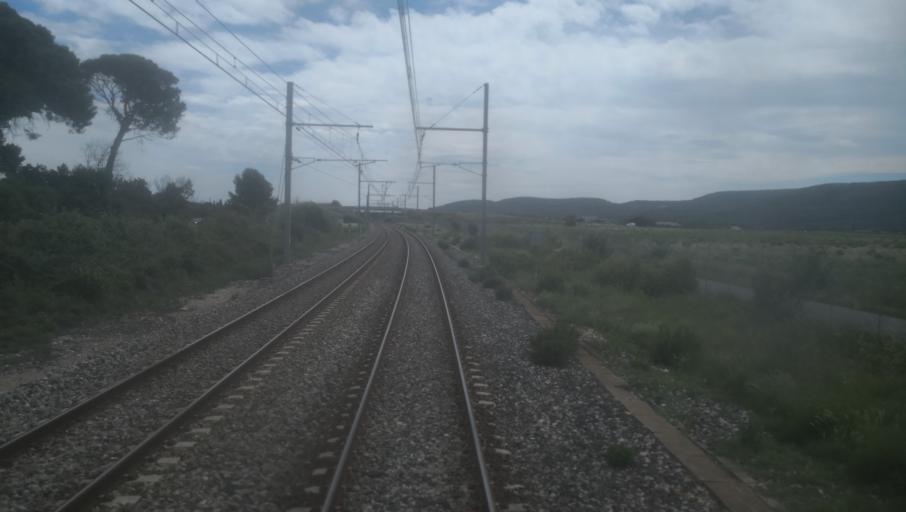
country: FR
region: Languedoc-Roussillon
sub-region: Departement de l'Herault
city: Vic-la-Gardiole
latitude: 43.4983
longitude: 3.7964
